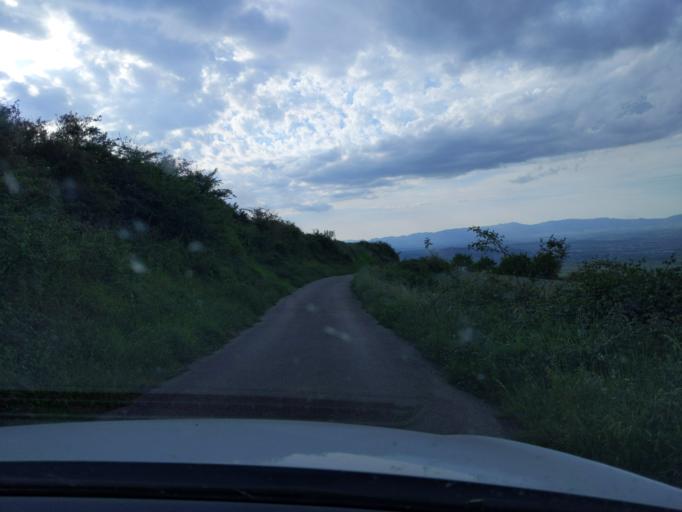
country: ES
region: La Rioja
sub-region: Provincia de La Rioja
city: Clavijo
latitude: 42.3515
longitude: -2.4315
